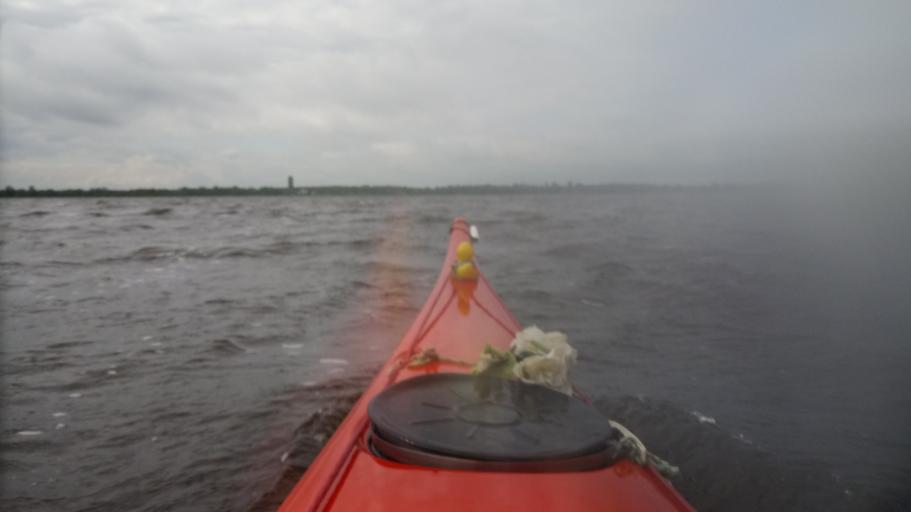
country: NL
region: Overijssel
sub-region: Gemeente Steenwijkerland
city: Sint Jansklooster
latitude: 52.6924
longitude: 6.0227
